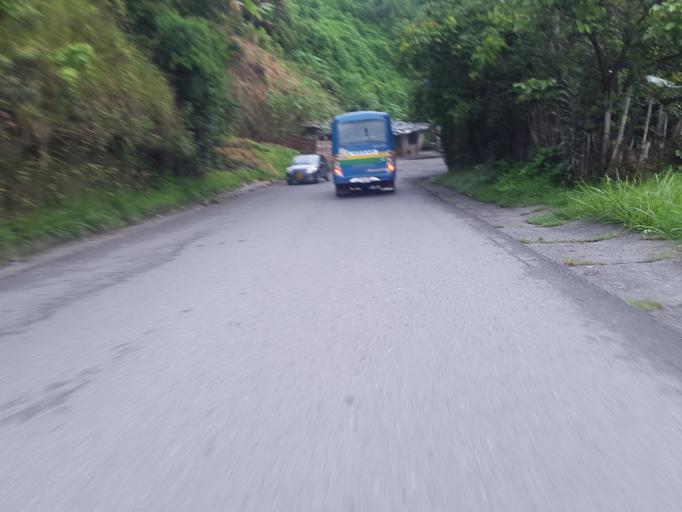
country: CO
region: Quindio
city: Armenia
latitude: 4.5324
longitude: -75.6696
